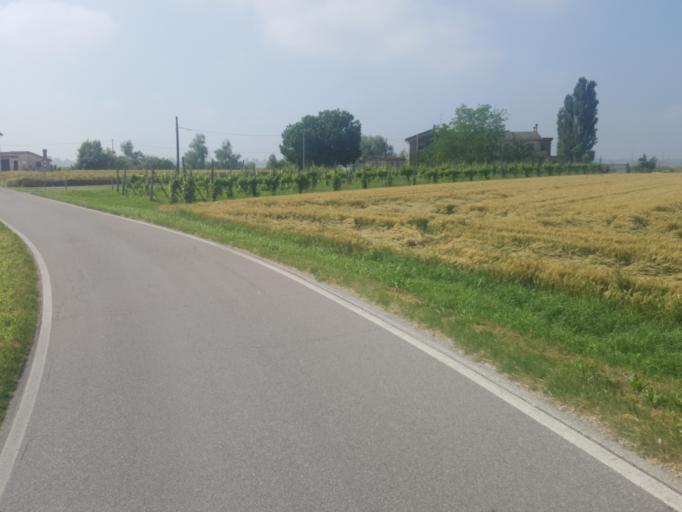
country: IT
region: Veneto
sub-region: Provincia di Rovigo
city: Canaro
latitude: 44.9354
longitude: 11.6504
